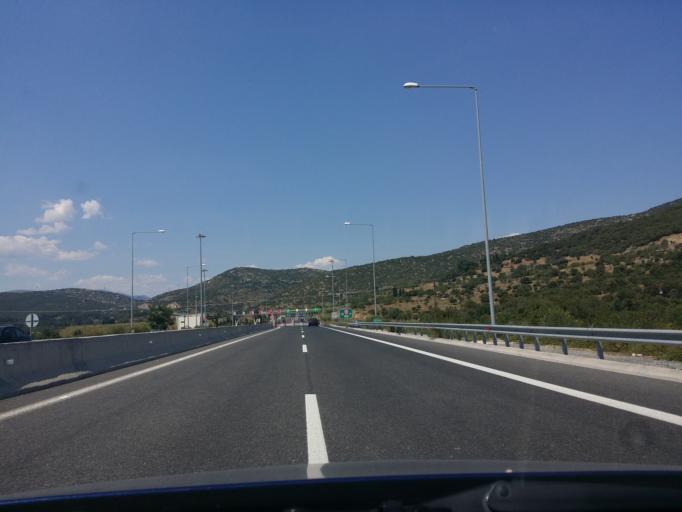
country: GR
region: Peloponnese
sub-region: Nomos Arkadias
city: Tripoli
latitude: 37.4091
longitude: 22.3068
